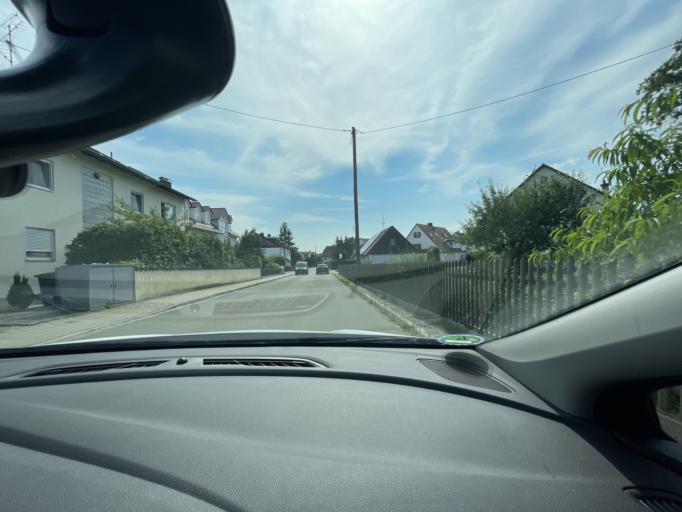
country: DE
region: Bavaria
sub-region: Upper Bavaria
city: Rohrmoos
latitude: 48.3231
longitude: 11.4144
